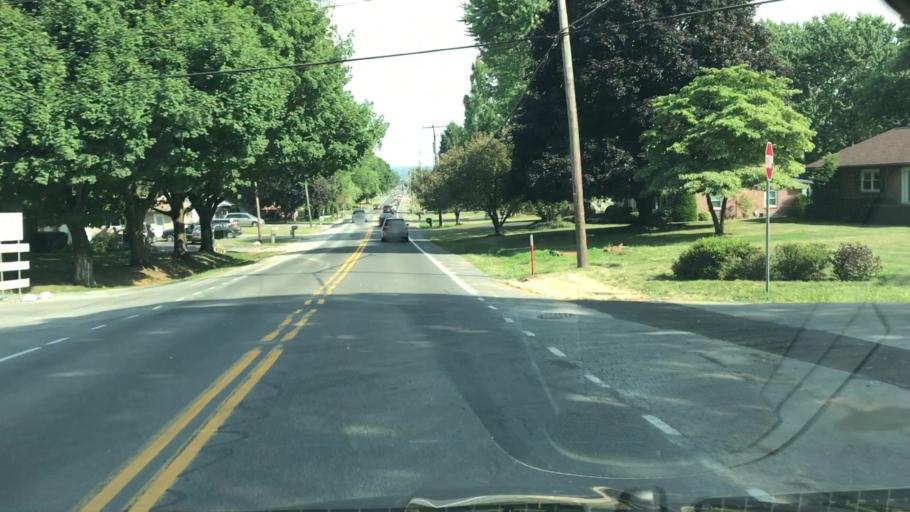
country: US
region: Pennsylvania
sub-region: Cumberland County
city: Carlisle
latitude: 40.1868
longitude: -77.1584
